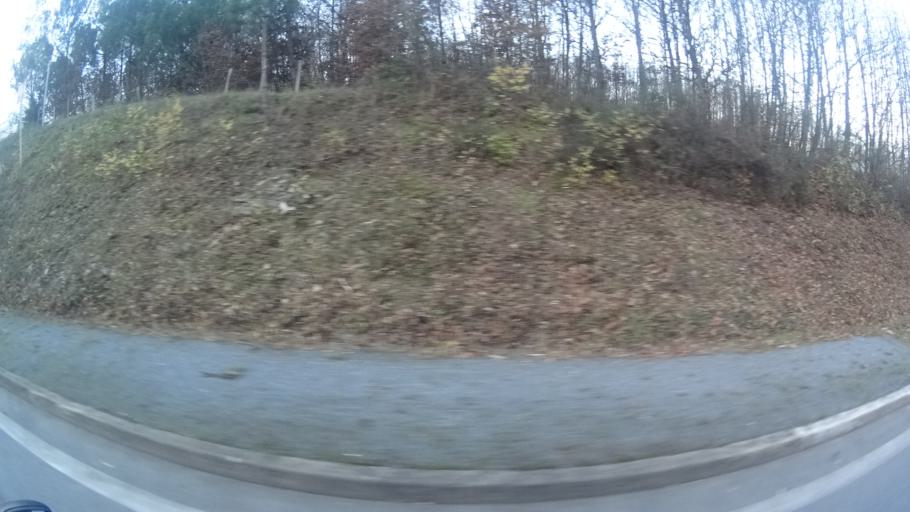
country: FR
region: Pays de la Loire
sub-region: Departement de la Loire-Atlantique
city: Saint-Nicolas-de-Redon
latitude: 47.6447
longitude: -2.0511
